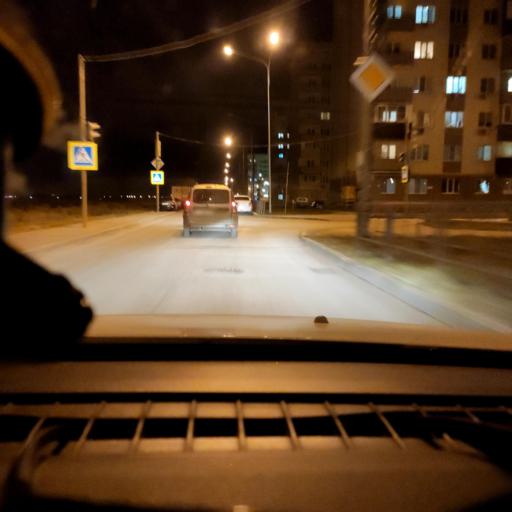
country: RU
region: Samara
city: Samara
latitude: 53.1135
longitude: 50.1414
